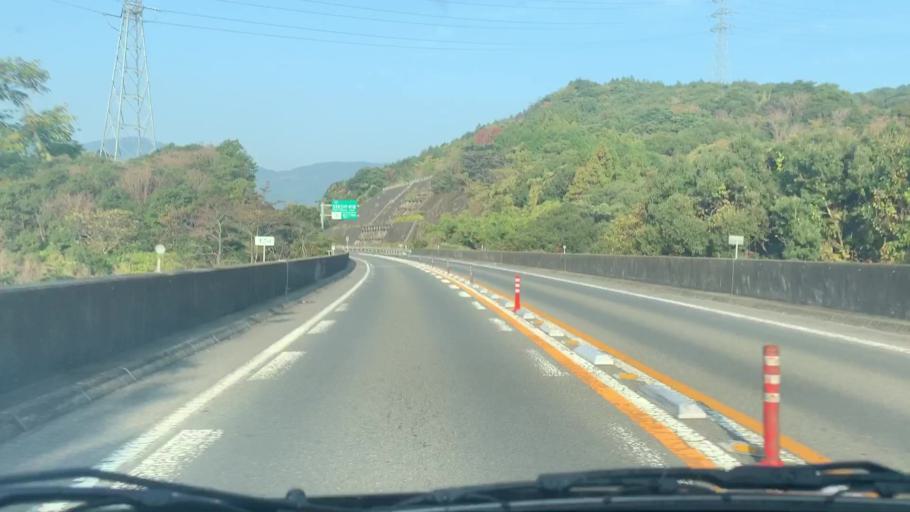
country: JP
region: Saga Prefecture
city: Imaricho-ko
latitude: 33.1650
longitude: 129.8614
